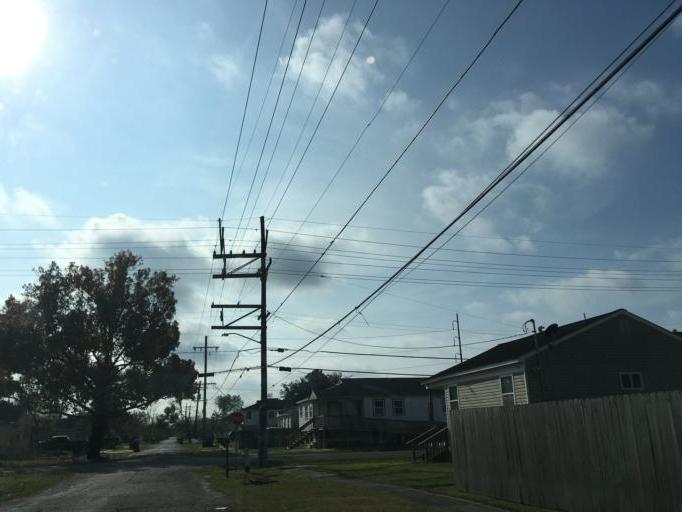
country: US
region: Louisiana
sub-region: Orleans Parish
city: New Orleans
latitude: 29.9904
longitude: -90.0550
